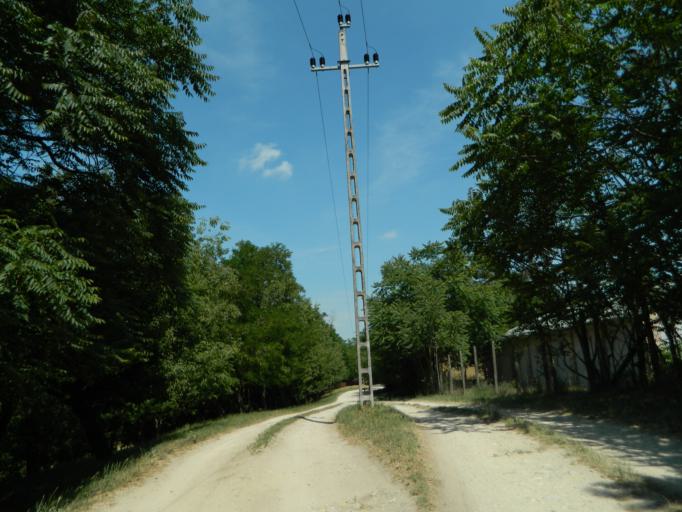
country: HU
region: Somogy
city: Balatonfoldvar
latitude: 46.8245
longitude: 17.9017
